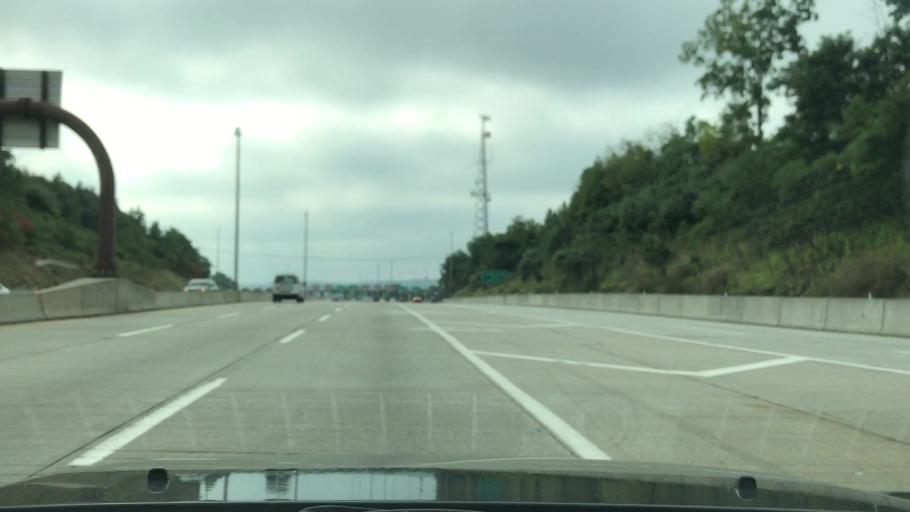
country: US
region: Pennsylvania
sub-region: Montgomery County
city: King of Prussia
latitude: 40.0899
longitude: -75.4070
